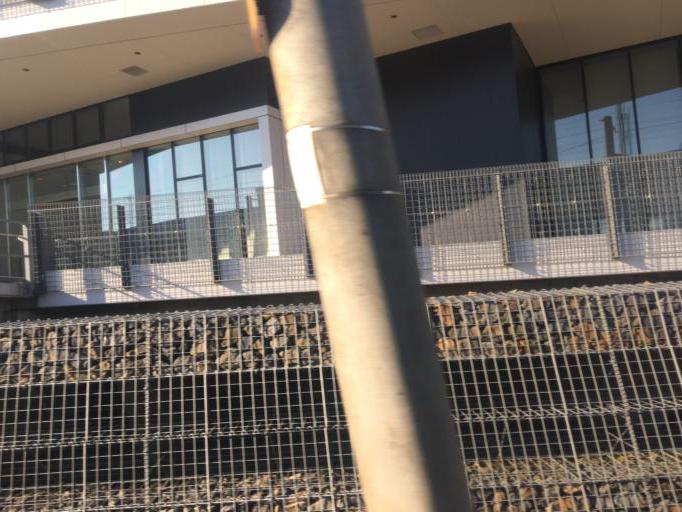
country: JP
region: Gunma
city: Takasaki
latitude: 36.3162
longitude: 139.0133
